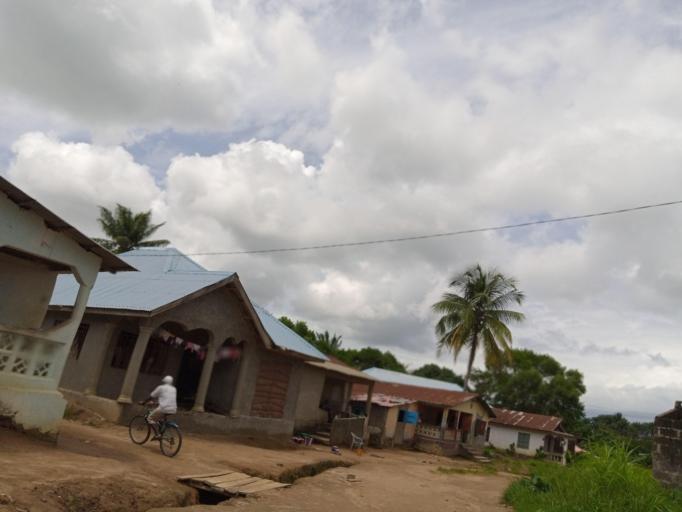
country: SL
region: Northern Province
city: Masoyila
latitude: 8.5933
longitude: -13.1837
